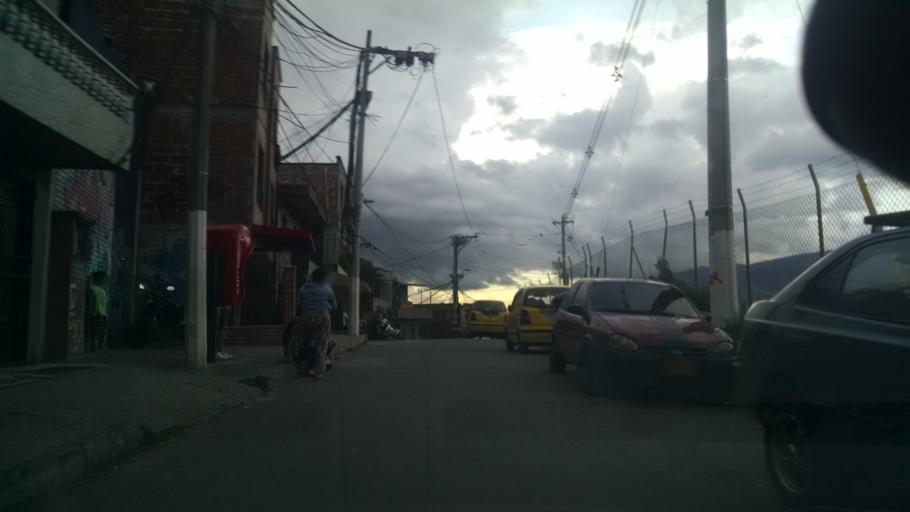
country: CO
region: Antioquia
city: Medellin
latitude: 6.2722
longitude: -75.6115
